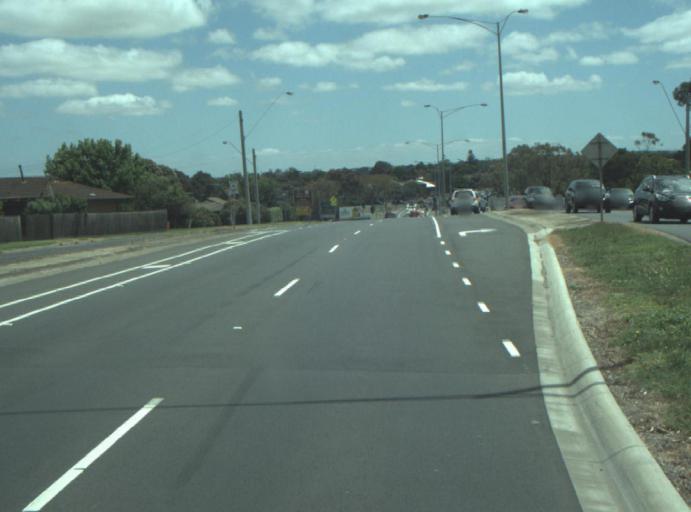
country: AU
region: Victoria
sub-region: Greater Geelong
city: Breakwater
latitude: -38.1816
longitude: 144.3488
